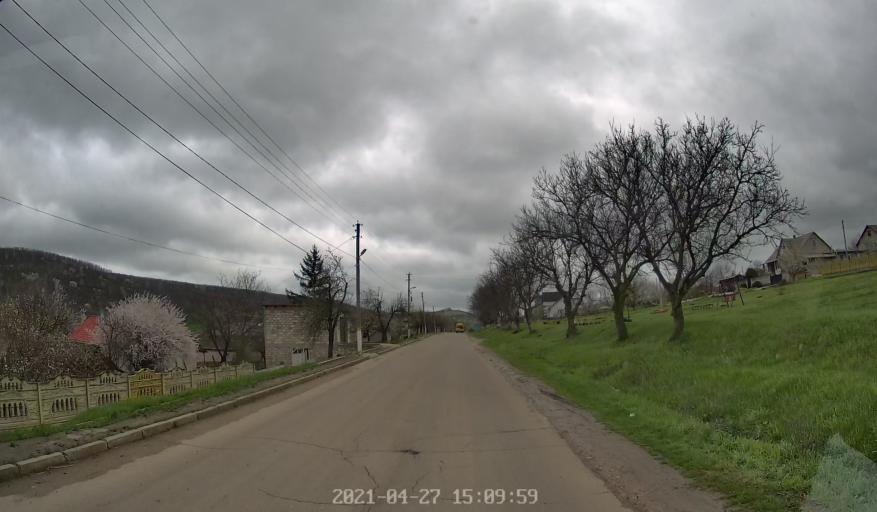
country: MD
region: Chisinau
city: Vadul lui Voda
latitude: 47.0447
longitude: 29.0334
